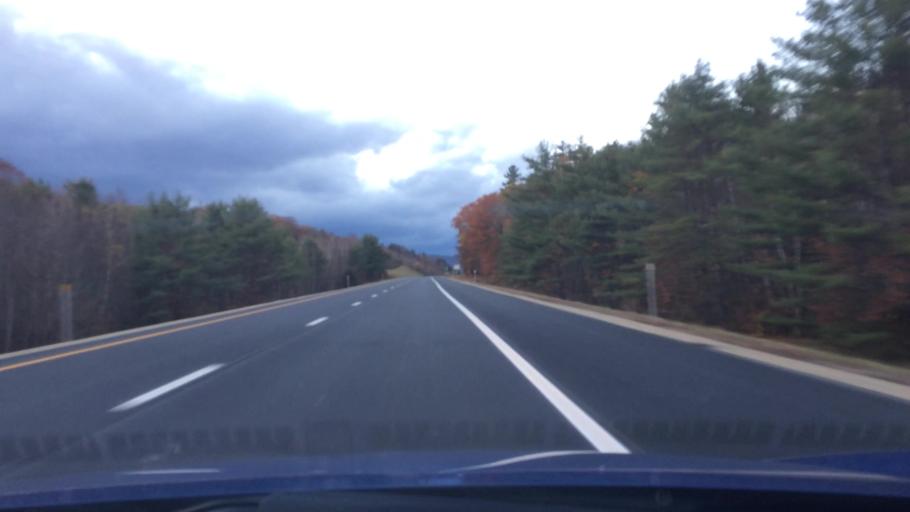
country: US
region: New Hampshire
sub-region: Grafton County
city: Thornton
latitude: 43.8833
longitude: -71.6778
